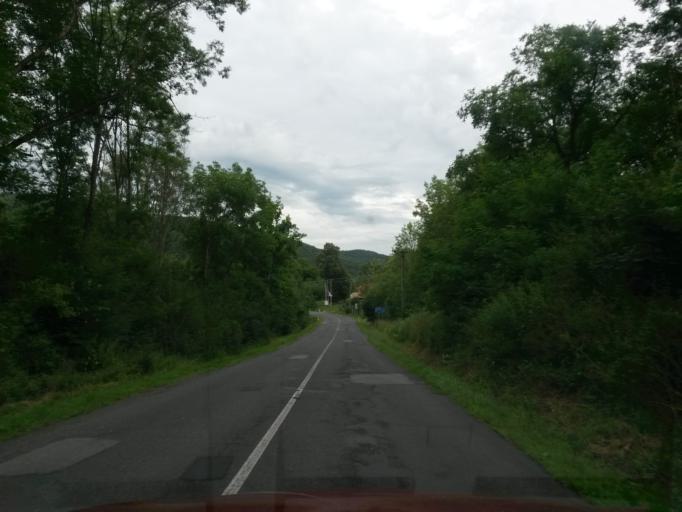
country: SK
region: Banskobystricky
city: Velky Krtis
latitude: 48.3560
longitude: 19.4047
